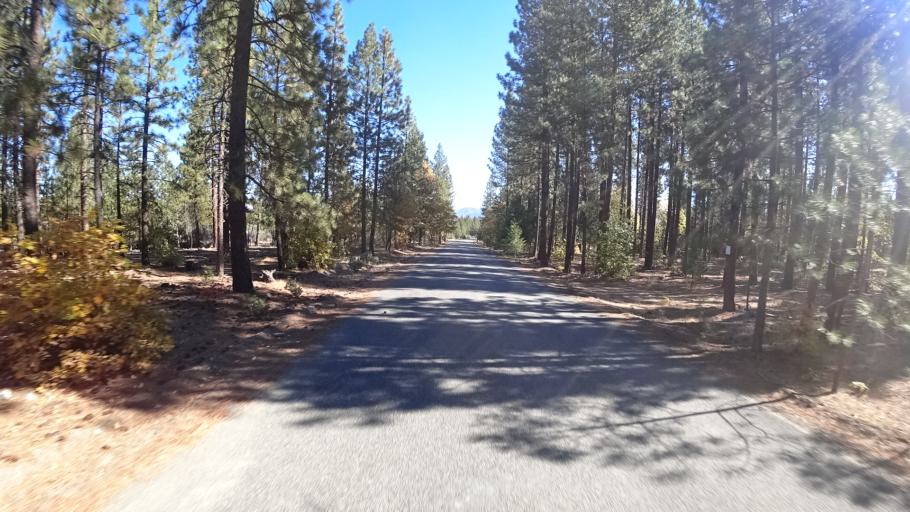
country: US
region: California
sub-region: Siskiyou County
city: Yreka
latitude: 41.5118
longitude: -122.9211
